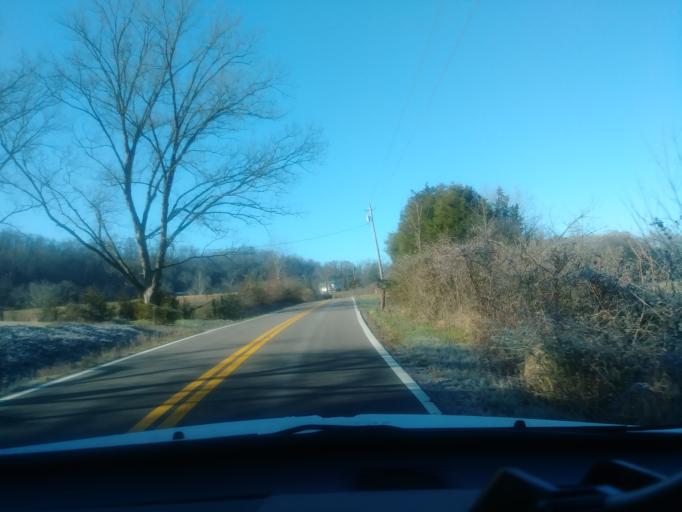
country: US
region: Tennessee
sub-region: Greene County
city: Mosheim
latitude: 36.1215
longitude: -83.0663
